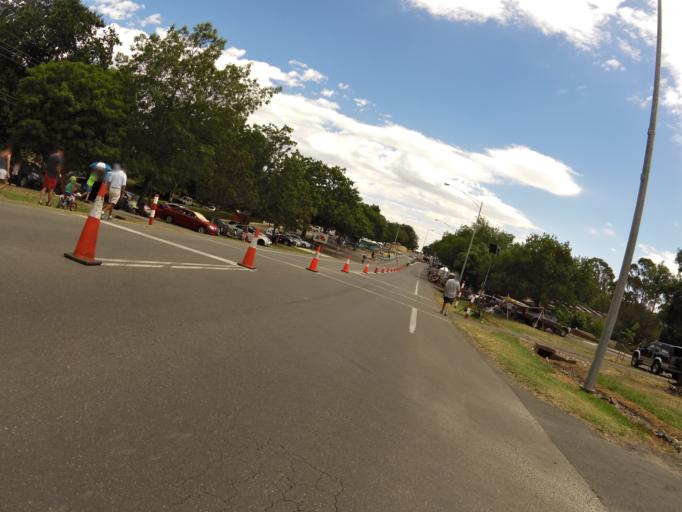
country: AU
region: Victoria
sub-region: Ballarat North
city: Mount Clear
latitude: -37.6508
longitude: 143.8865
